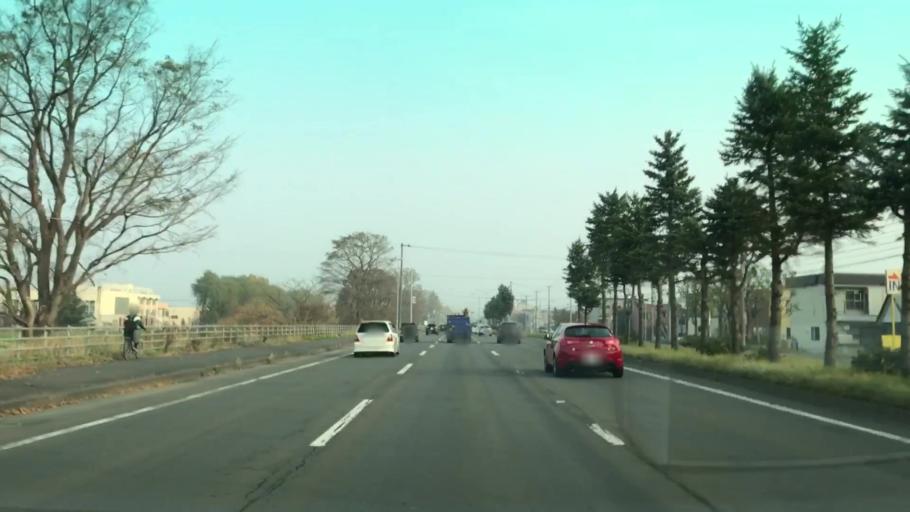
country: JP
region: Hokkaido
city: Sapporo
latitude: 43.1513
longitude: 141.3511
